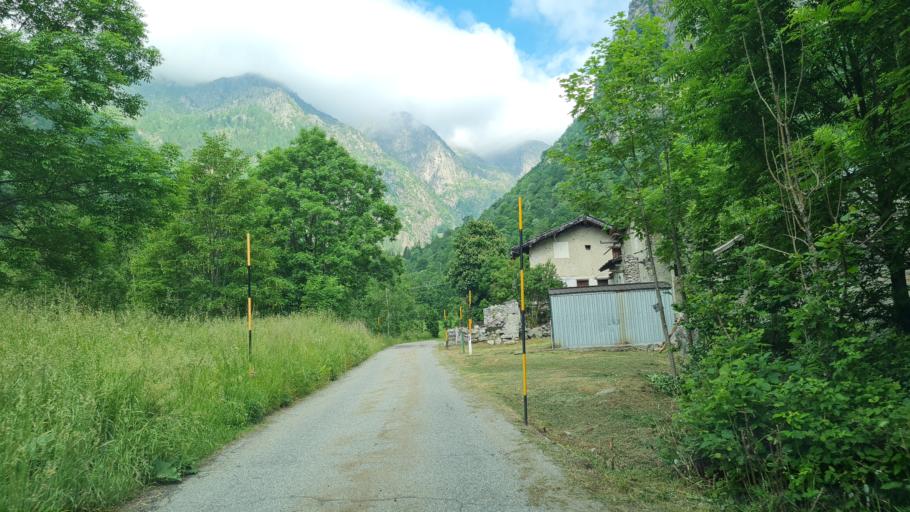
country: IT
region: Piedmont
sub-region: Provincia di Torino
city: Locana
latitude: 45.4544
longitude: 7.3963
